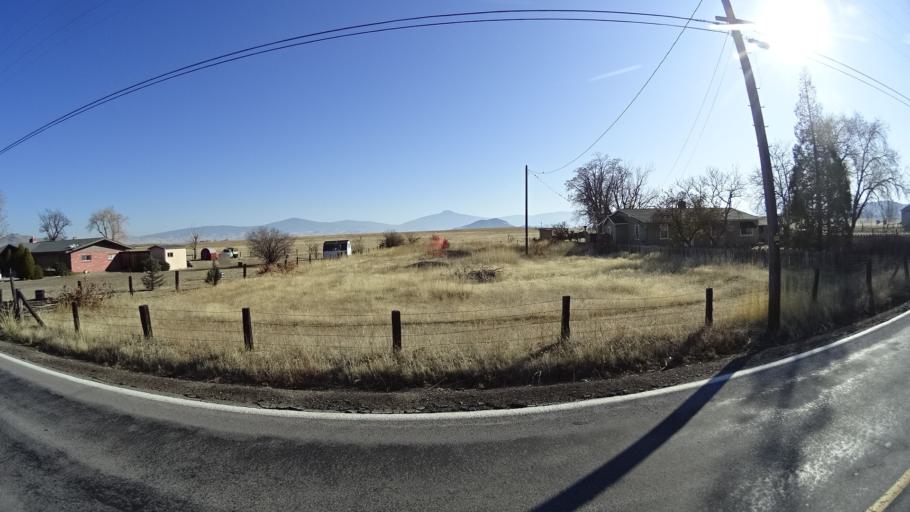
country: US
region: California
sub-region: Siskiyou County
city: Yreka
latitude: 41.7207
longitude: -122.5934
